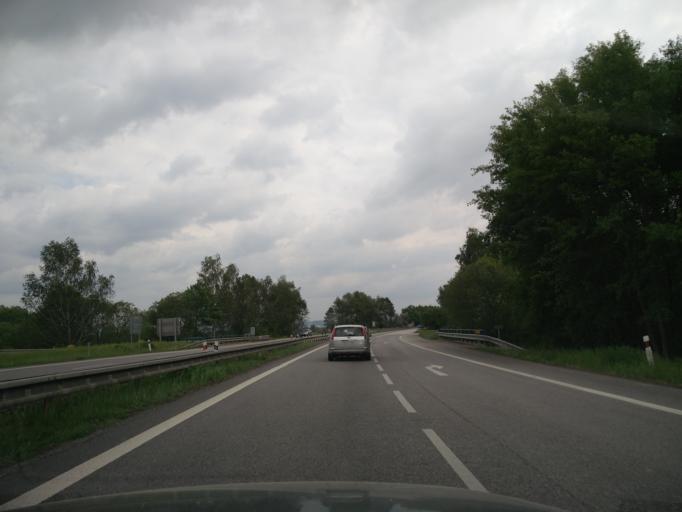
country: CZ
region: Jihocesky
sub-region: Okres Ceske Budejovice
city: Hluboka nad Vltavou
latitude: 49.0155
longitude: 14.4365
